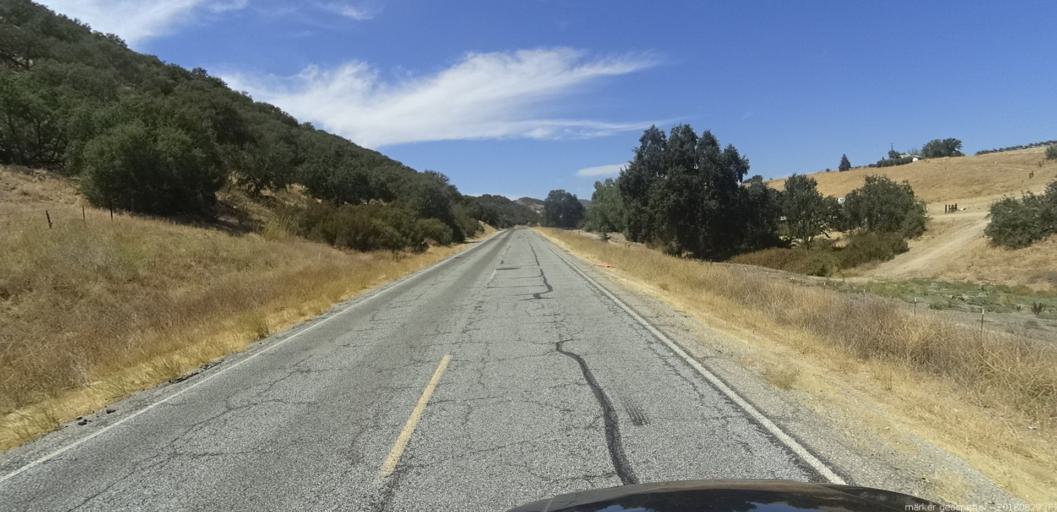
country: US
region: California
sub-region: San Luis Obispo County
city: Lake Nacimiento
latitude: 35.8894
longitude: -120.9263
